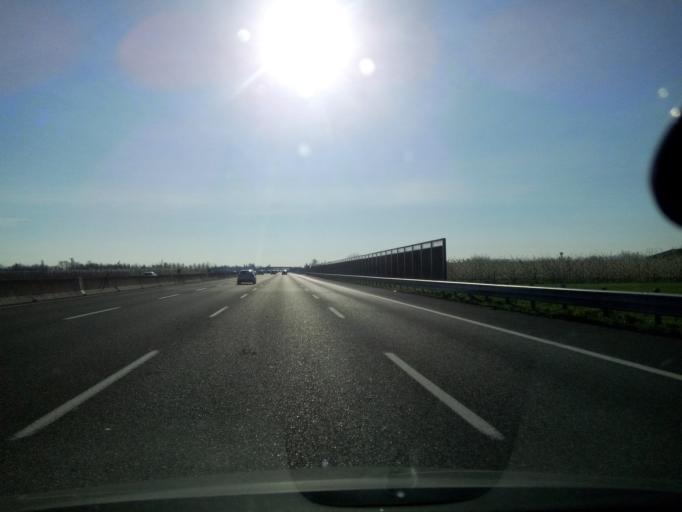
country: IT
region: Emilia-Romagna
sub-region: Provincia di Modena
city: San Cesario sul Panaro
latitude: 44.5706
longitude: 11.0156
